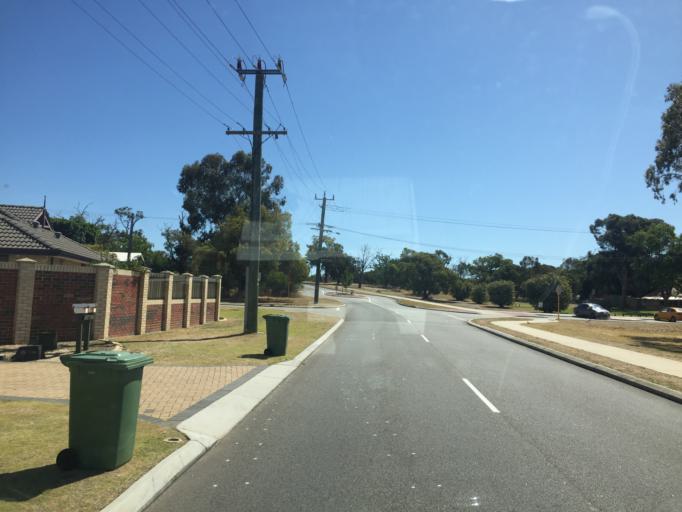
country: AU
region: Western Australia
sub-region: Belmont
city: Redcliffe
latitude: -31.9355
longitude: 115.9470
